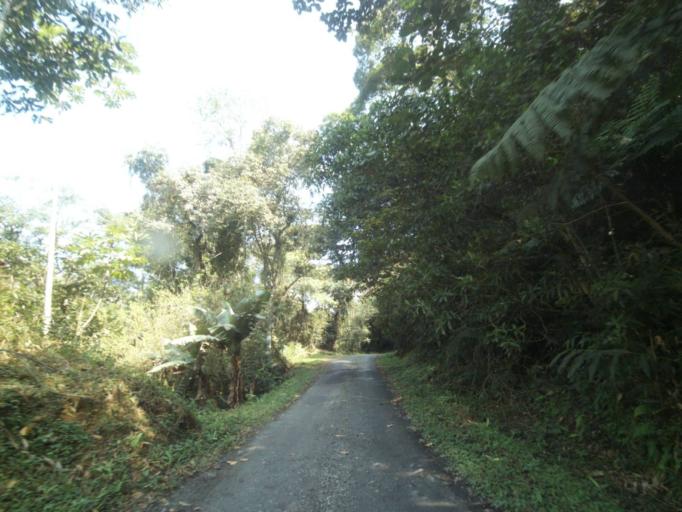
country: BR
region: Parana
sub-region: Paranagua
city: Paranagua
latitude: -25.5585
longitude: -48.6498
